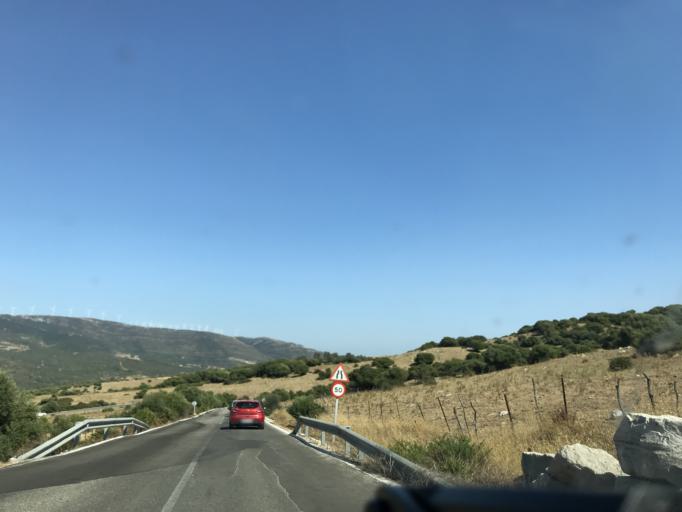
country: ES
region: Andalusia
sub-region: Provincia de Cadiz
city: Zahara de los Atunes
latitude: 36.1018
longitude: -5.7228
